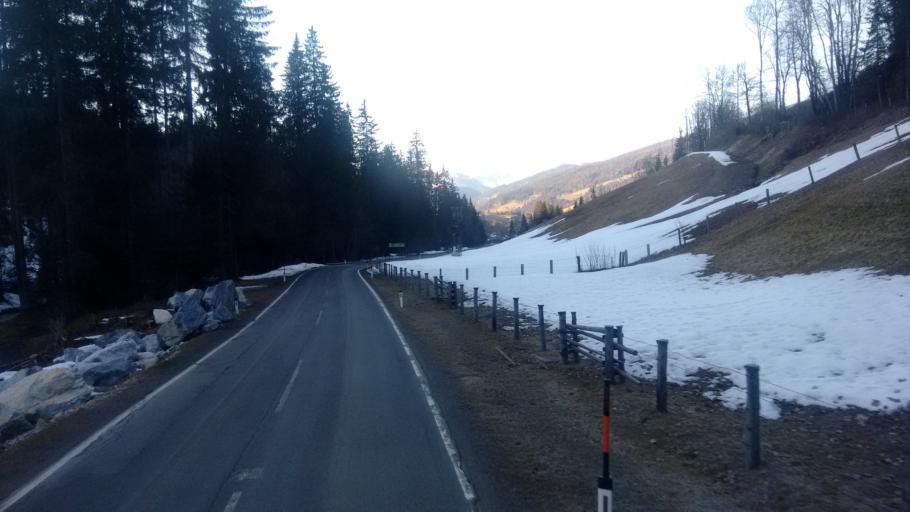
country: AT
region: Salzburg
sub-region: Politischer Bezirk Sankt Johann im Pongau
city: Altenmarkt im Pongau
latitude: 47.3541
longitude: 13.4286
